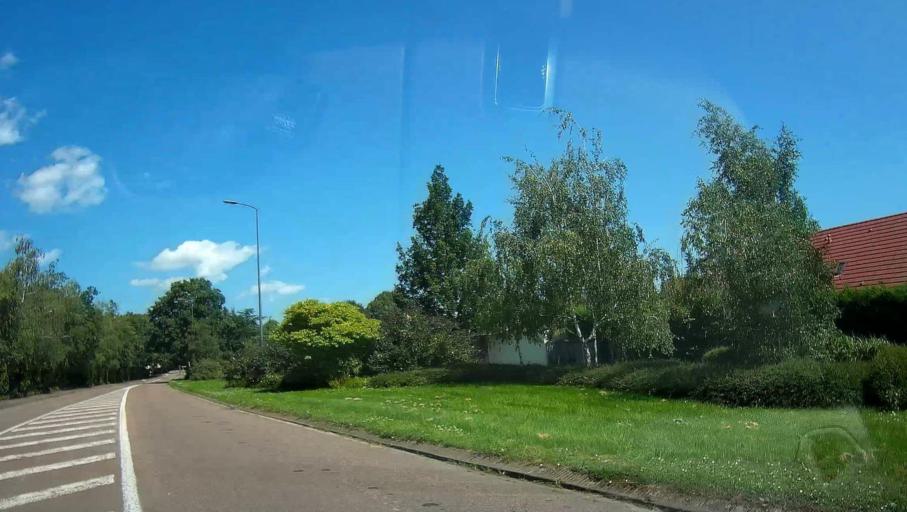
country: FR
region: Bourgogne
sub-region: Departement de la Cote-d'Or
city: Beaune
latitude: 47.0181
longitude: 4.8357
